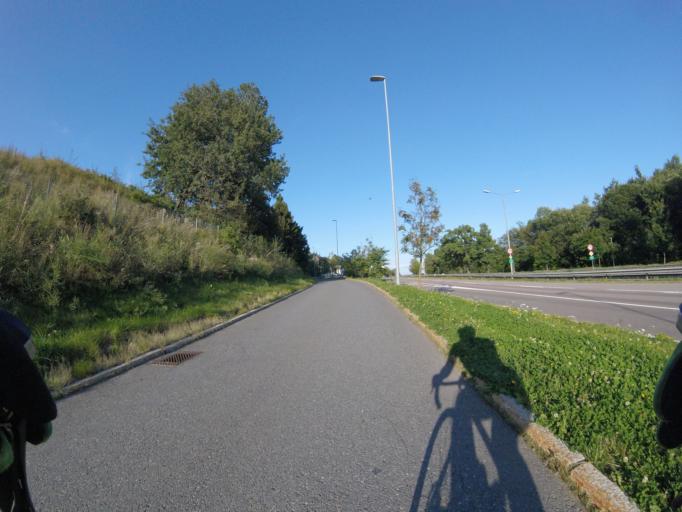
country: NO
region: Oslo
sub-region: Oslo
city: Oslo
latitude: 59.9435
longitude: 10.8300
